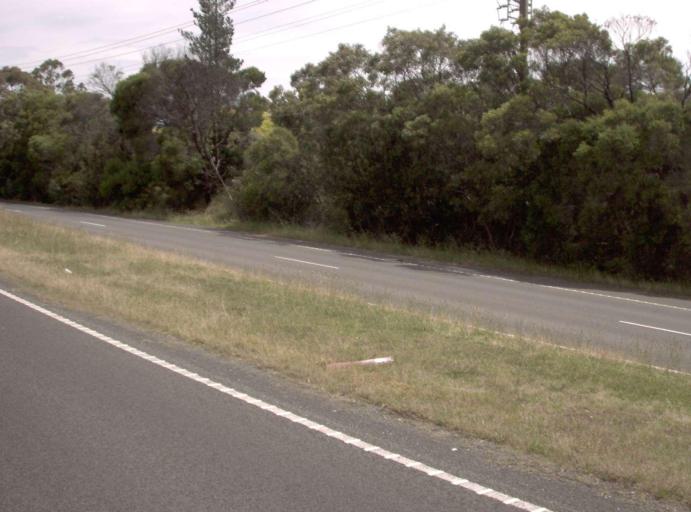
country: AU
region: Victoria
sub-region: Frankston
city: Frankston South
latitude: -38.1835
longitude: 145.1403
